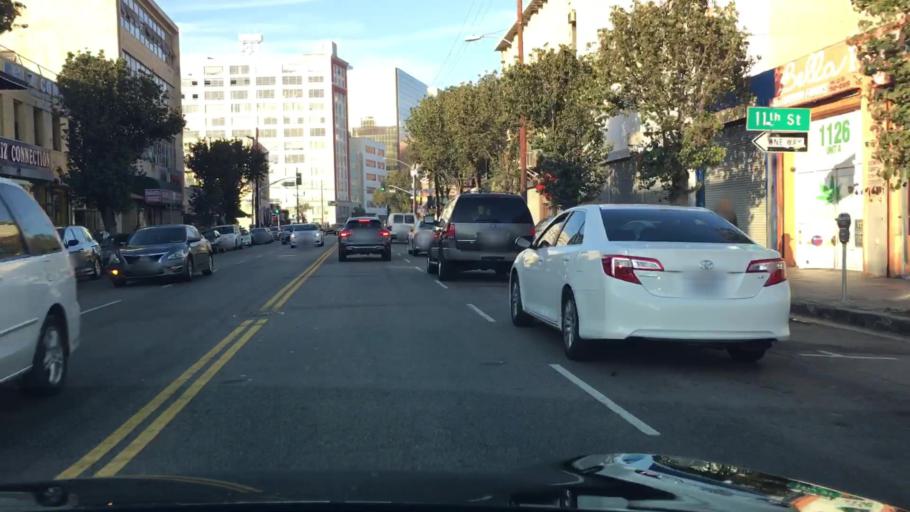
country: US
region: California
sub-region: Los Angeles County
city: Los Angeles
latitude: 34.0376
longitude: -118.2578
